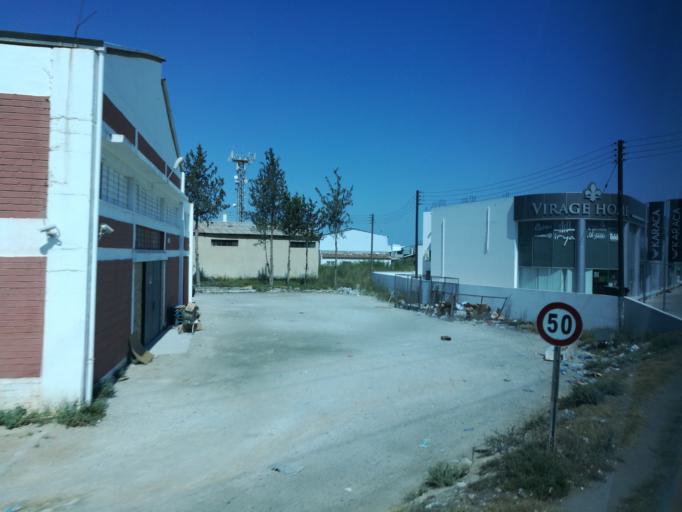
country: CY
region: Ammochostos
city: Famagusta
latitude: 35.1423
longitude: 33.9045
